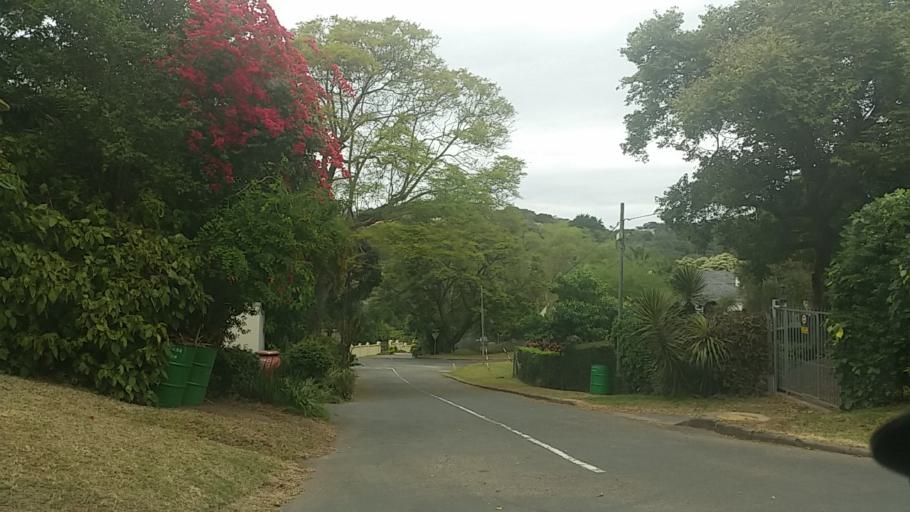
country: ZA
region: KwaZulu-Natal
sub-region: eThekwini Metropolitan Municipality
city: Berea
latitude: -29.8383
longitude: 30.9314
